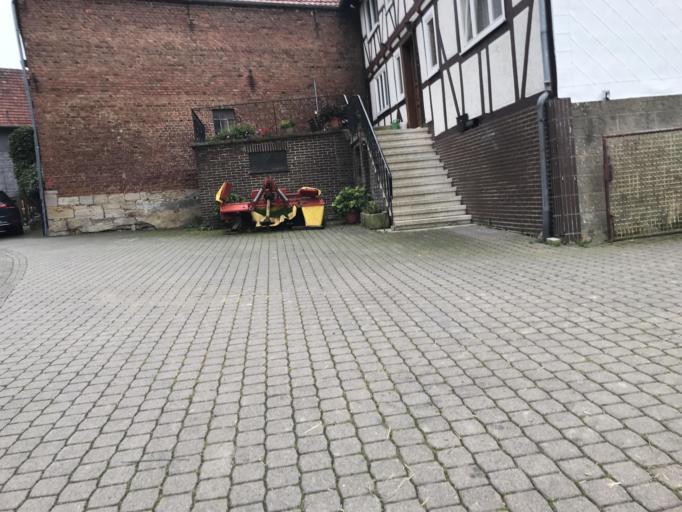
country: DE
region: Hesse
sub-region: Regierungsbezirk Kassel
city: Guxhagen
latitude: 51.2109
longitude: 9.4430
